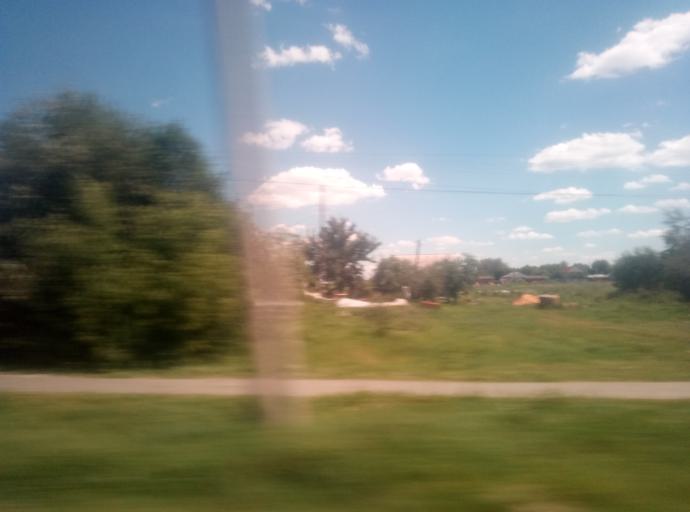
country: RU
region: Tula
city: Kireyevsk
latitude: 53.9854
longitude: 37.9327
